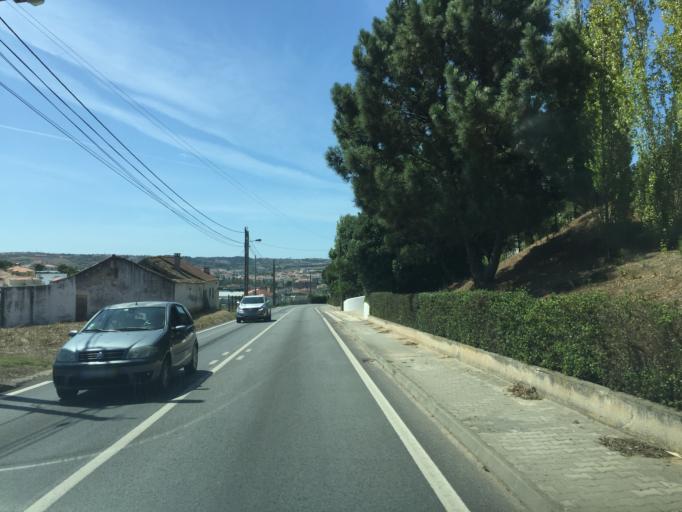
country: PT
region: Lisbon
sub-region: Lourinha
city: Lourinha
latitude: 39.2549
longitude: -9.3126
